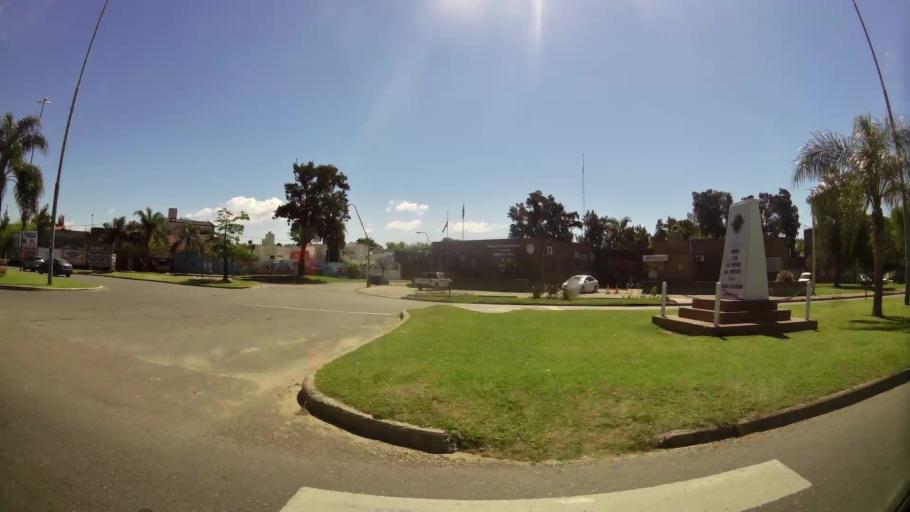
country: AR
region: Santa Fe
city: Santa Fe de la Vera Cruz
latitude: -31.6291
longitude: -60.6781
